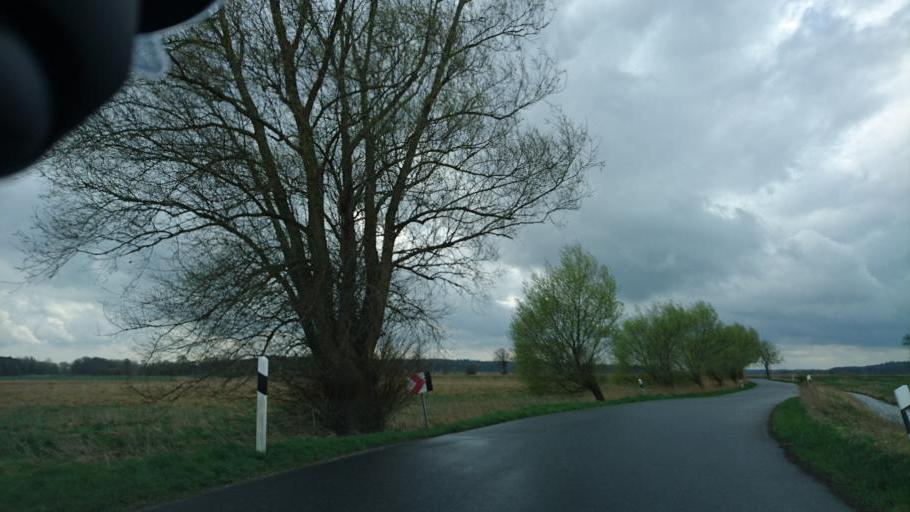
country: DE
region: Mecklenburg-Vorpommern
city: Bad Sulze
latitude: 54.1063
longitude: 12.6750
